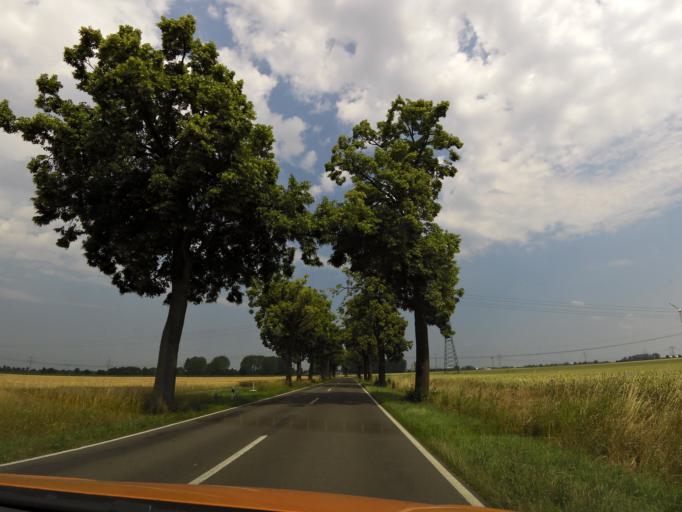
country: DE
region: Brandenburg
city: Nauen
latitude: 52.5843
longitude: 12.8757
